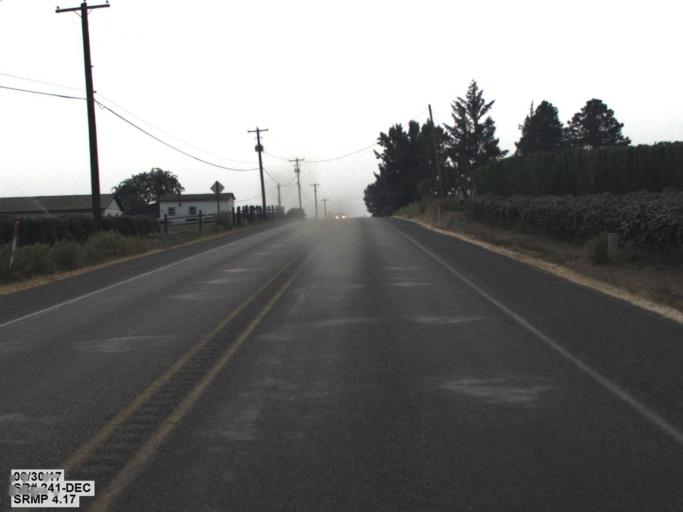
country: US
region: Washington
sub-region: Yakima County
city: Sunnyside
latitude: 46.2719
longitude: -119.9993
